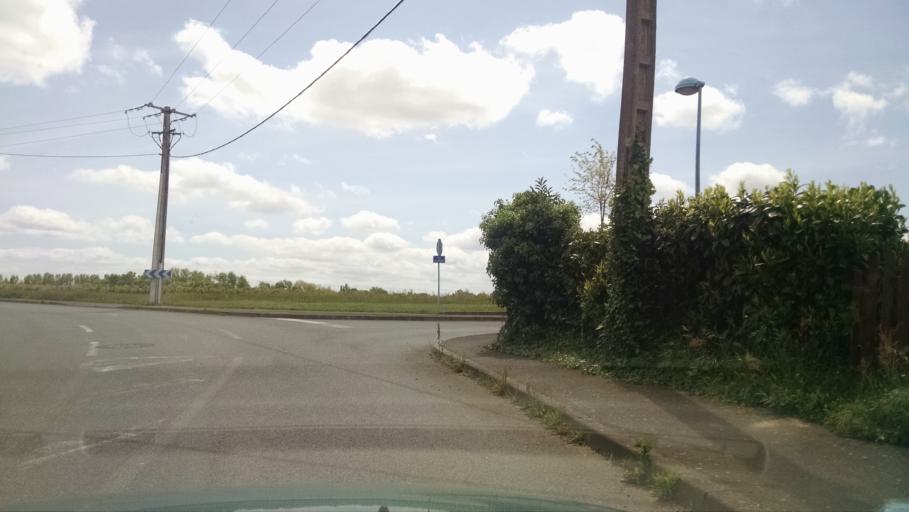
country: FR
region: Pays de la Loire
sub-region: Departement de la Loire-Atlantique
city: Gorges
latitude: 47.0906
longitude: -1.3103
